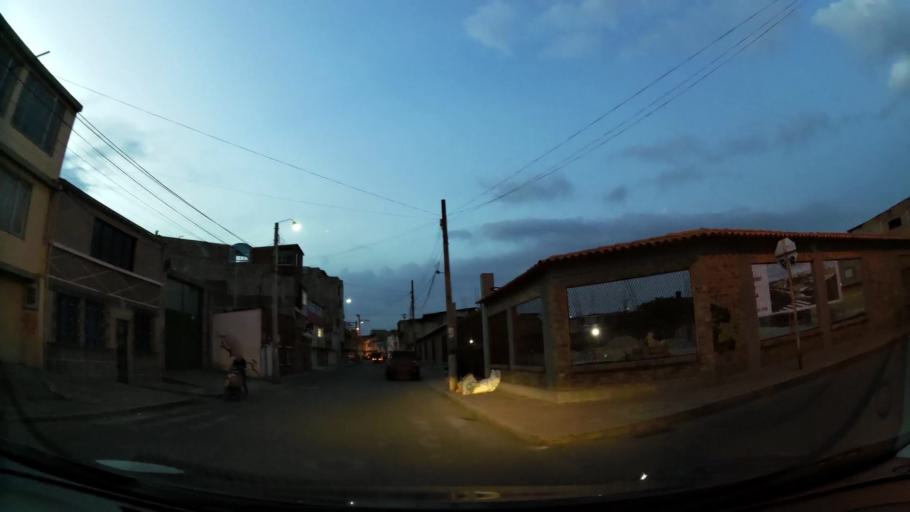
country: CO
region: Cundinamarca
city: Funza
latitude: 4.7166
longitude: -74.2144
